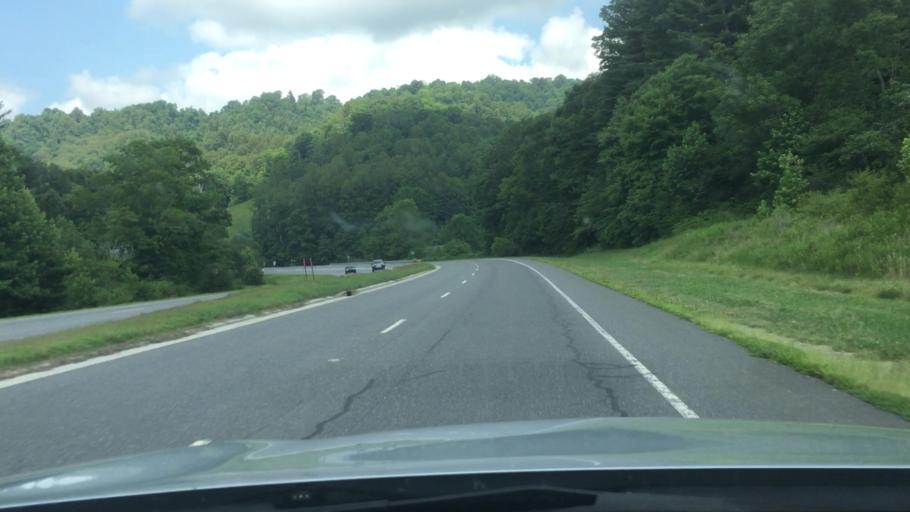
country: US
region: North Carolina
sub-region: Madison County
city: Mars Hill
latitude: 35.9144
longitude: -82.4587
